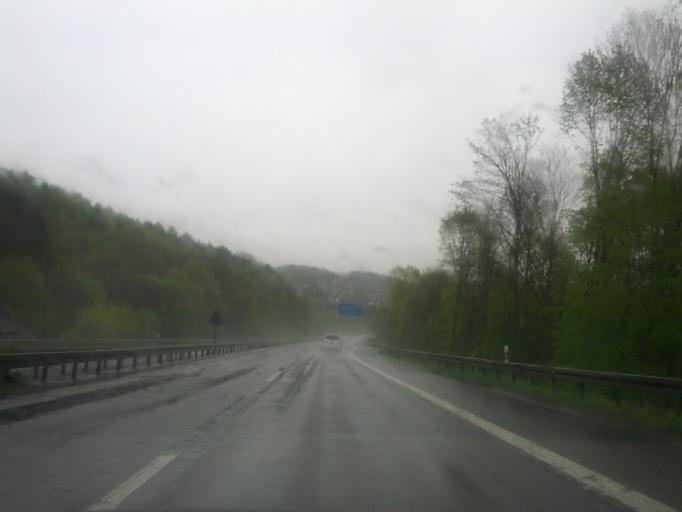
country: DE
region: North Rhine-Westphalia
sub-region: Regierungsbezirk Koln
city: Rosrath
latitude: 50.9496
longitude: 7.2098
